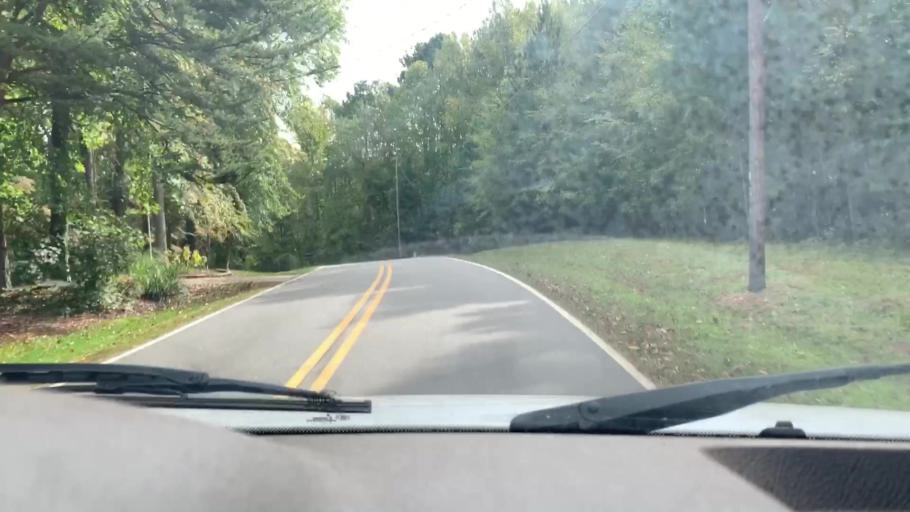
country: US
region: North Carolina
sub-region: Catawba County
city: Lake Norman of Catawba
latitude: 35.5733
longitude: -80.9464
